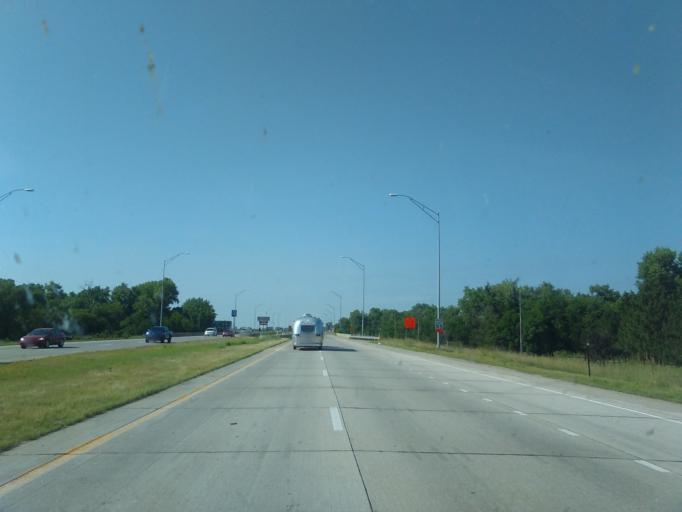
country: US
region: Nebraska
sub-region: Hall County
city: Grand Island
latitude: 40.8242
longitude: -98.3782
